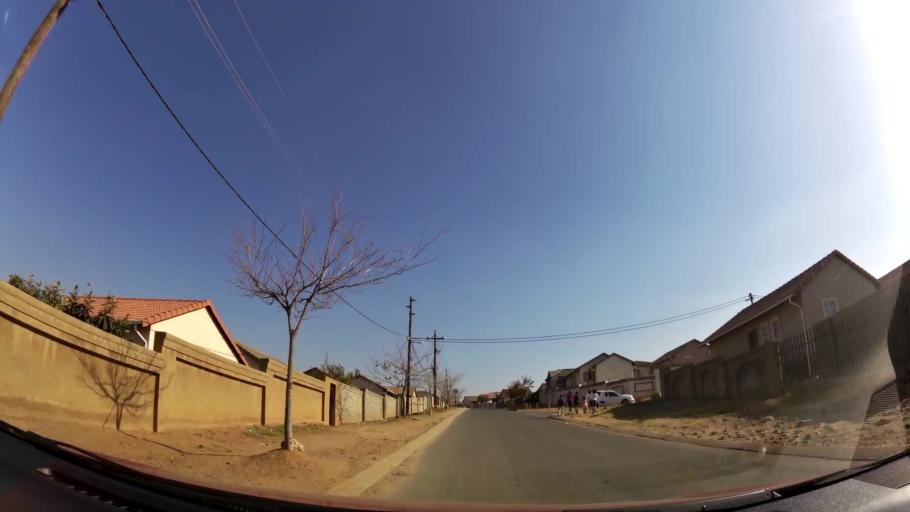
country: ZA
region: Gauteng
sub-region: West Rand District Municipality
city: Muldersdriseloop
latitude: -26.0319
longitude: 27.9171
